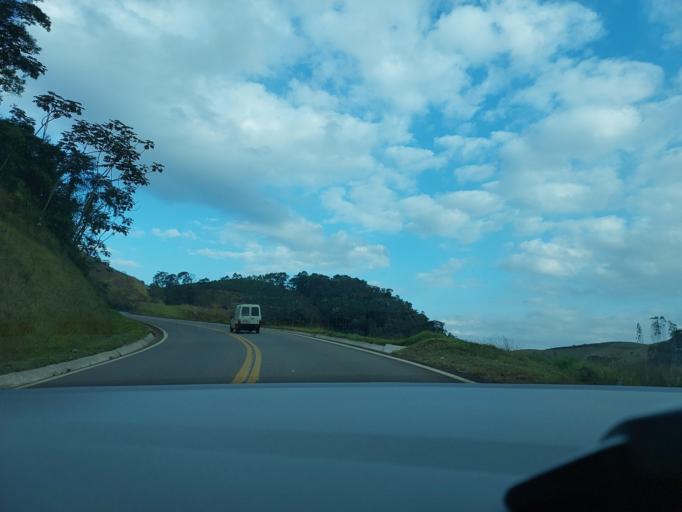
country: BR
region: Minas Gerais
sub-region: Mirai
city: Mirai
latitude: -21.0356
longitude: -42.5370
